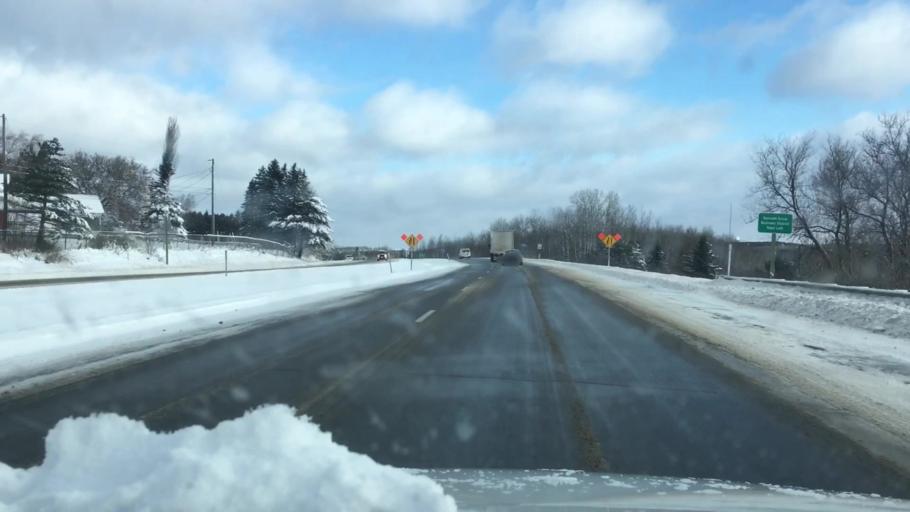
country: US
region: Maine
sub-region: Aroostook County
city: Caribou
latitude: 46.8637
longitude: -68.0007
